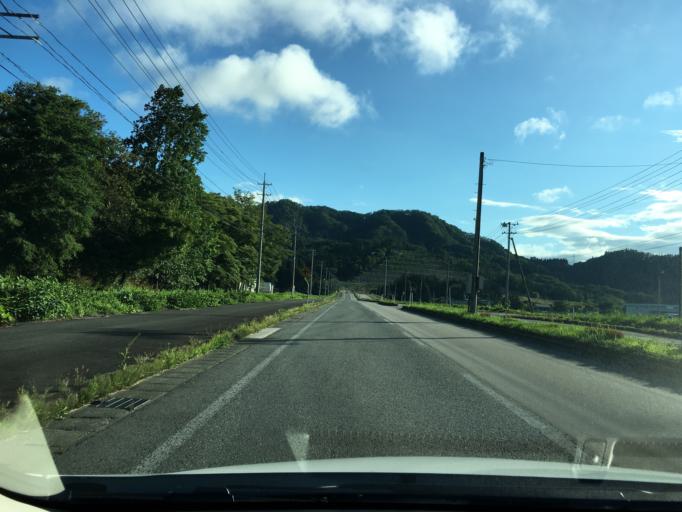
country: JP
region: Yamagata
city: Yonezawa
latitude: 37.8997
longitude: 140.1658
